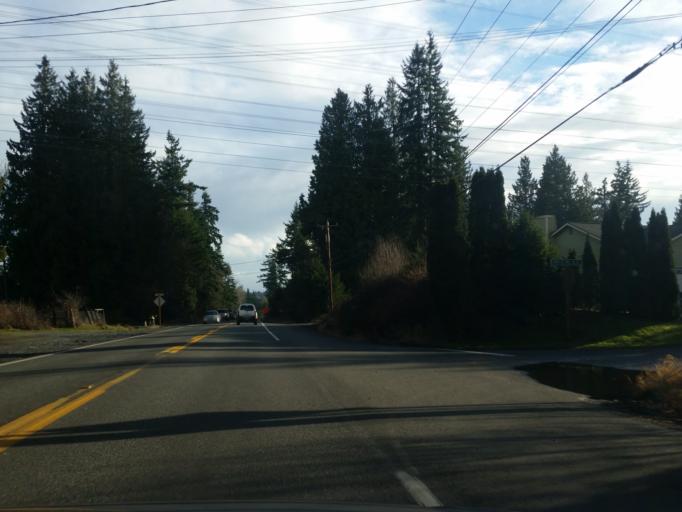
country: US
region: Washington
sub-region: Snohomish County
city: Martha Lake
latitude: 47.8172
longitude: -122.2304
